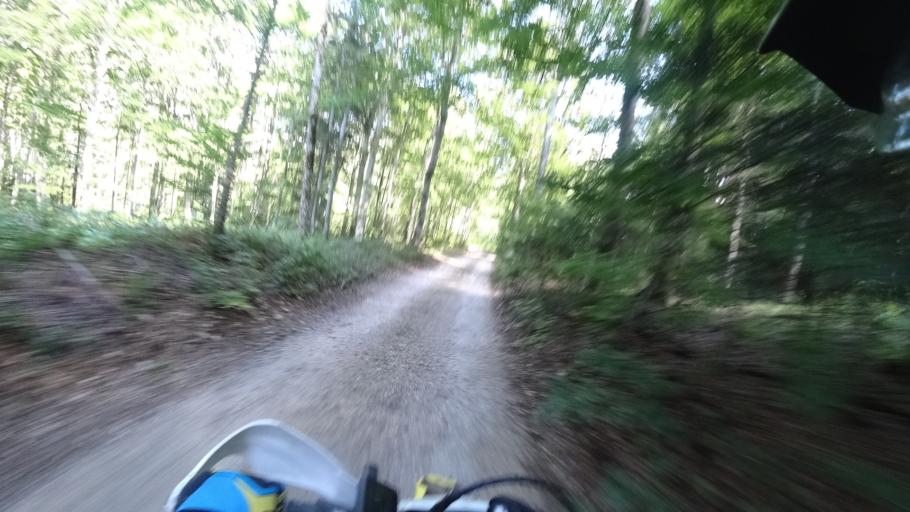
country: BA
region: Federation of Bosnia and Herzegovina
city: Orasac
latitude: 44.5004
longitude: 15.9473
